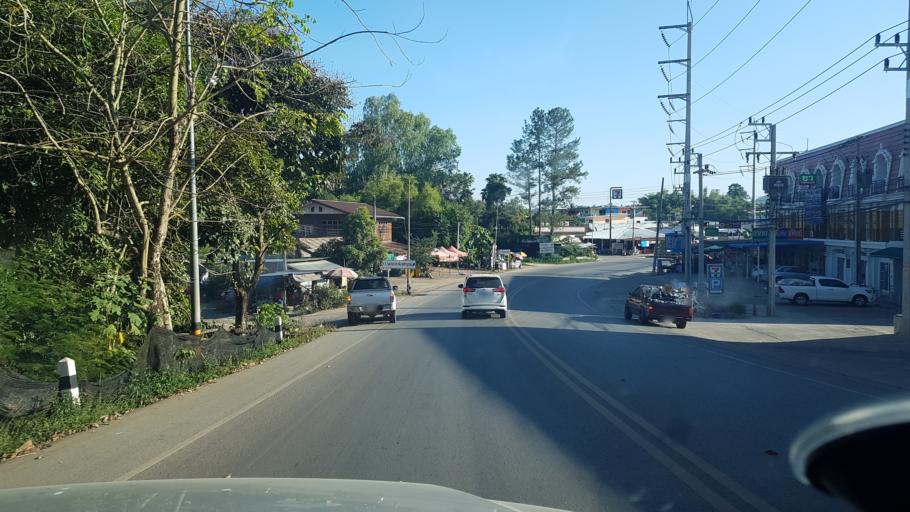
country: TH
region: Phetchabun
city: Khao Kho
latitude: 16.7087
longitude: 101.0398
